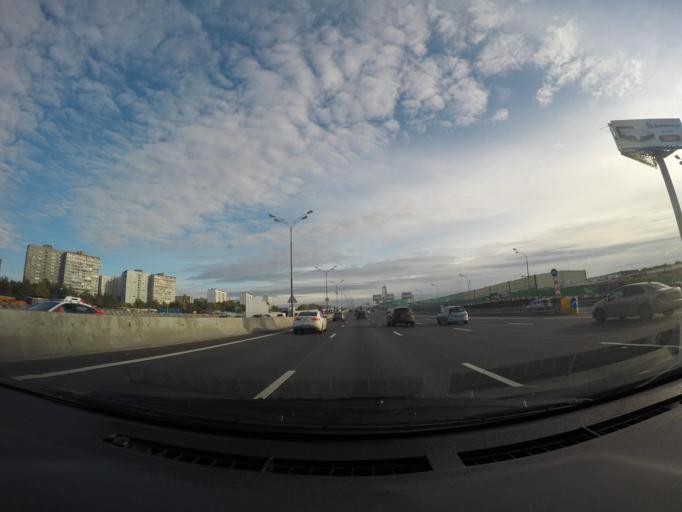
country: RU
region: Moscow
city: Tyoply Stan
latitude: 55.6180
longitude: 37.4839
